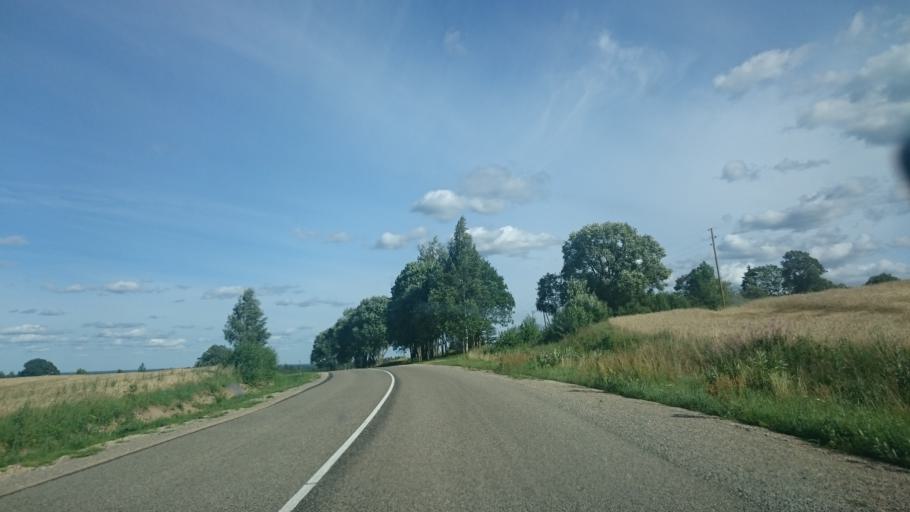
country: LV
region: Skrunda
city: Skrunda
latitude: 56.6841
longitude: 21.8952
